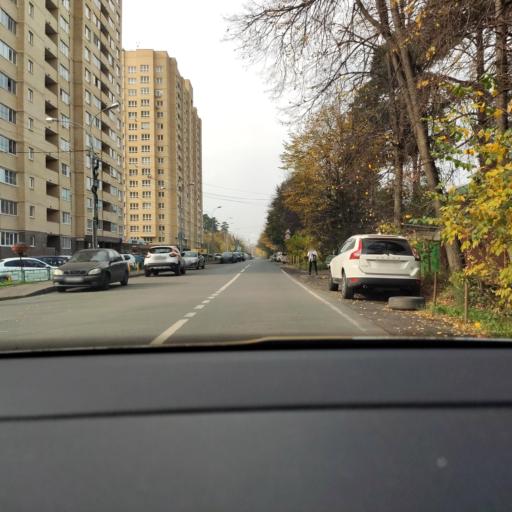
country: RU
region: Moskovskaya
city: Korolev
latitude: 55.9304
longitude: 37.7923
